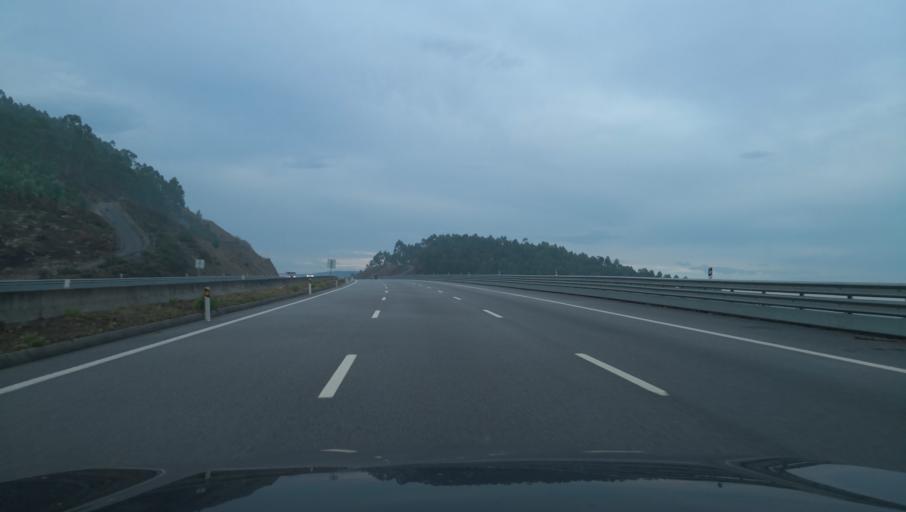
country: PT
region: Porto
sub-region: Paredes
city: Recarei
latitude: 41.1234
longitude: -8.4333
